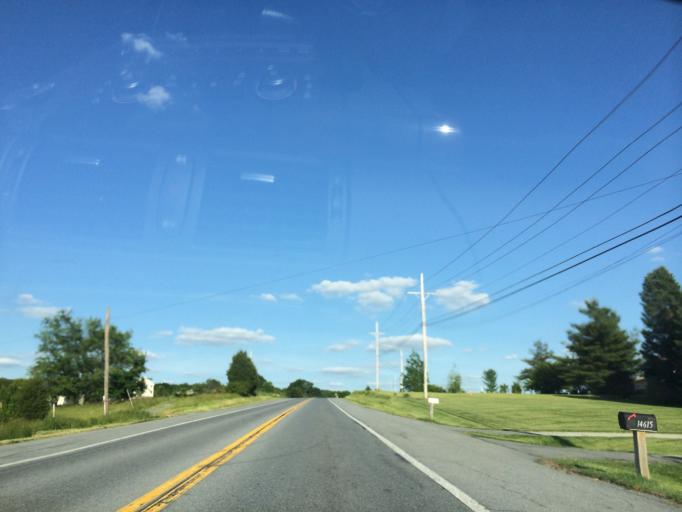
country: US
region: Maryland
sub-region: Frederick County
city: Linganore
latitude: 39.4697
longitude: -77.1527
